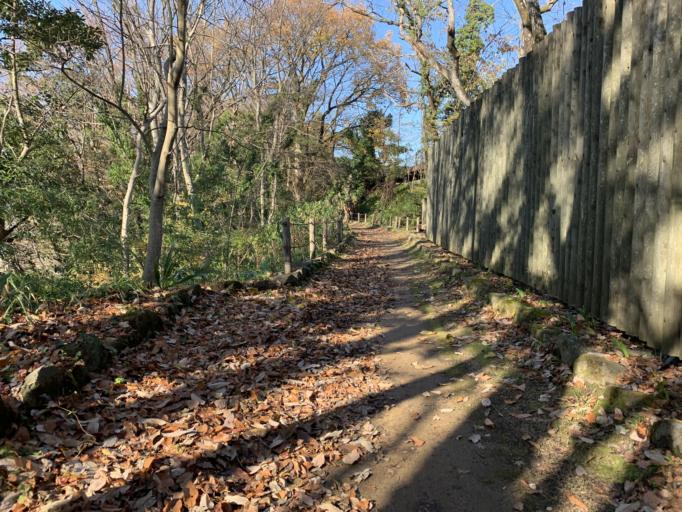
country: JP
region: Ishikawa
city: Nonoichi
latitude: 36.5385
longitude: 136.6867
